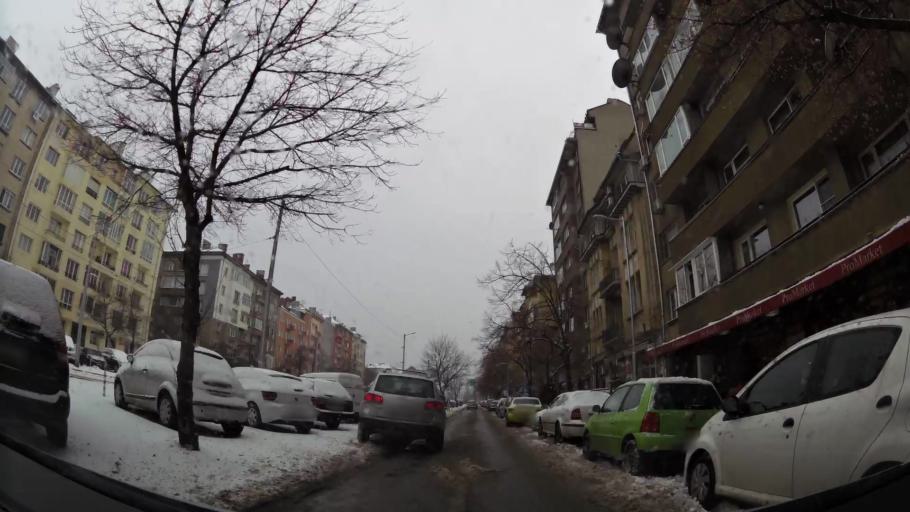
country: BG
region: Sofia-Capital
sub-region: Stolichna Obshtina
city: Sofia
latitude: 42.6937
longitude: 23.3128
